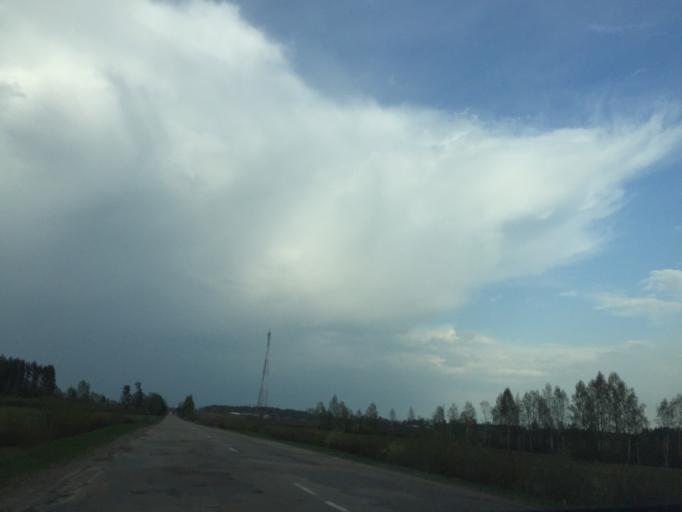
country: LV
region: Incukalns
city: Incukalns
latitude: 57.0249
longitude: 24.7840
